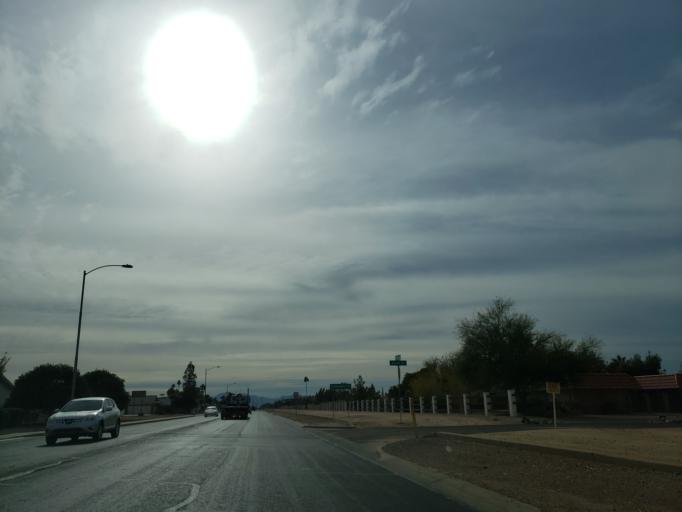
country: US
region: Arizona
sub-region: Maricopa County
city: Youngtown
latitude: 33.5771
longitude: -112.2988
